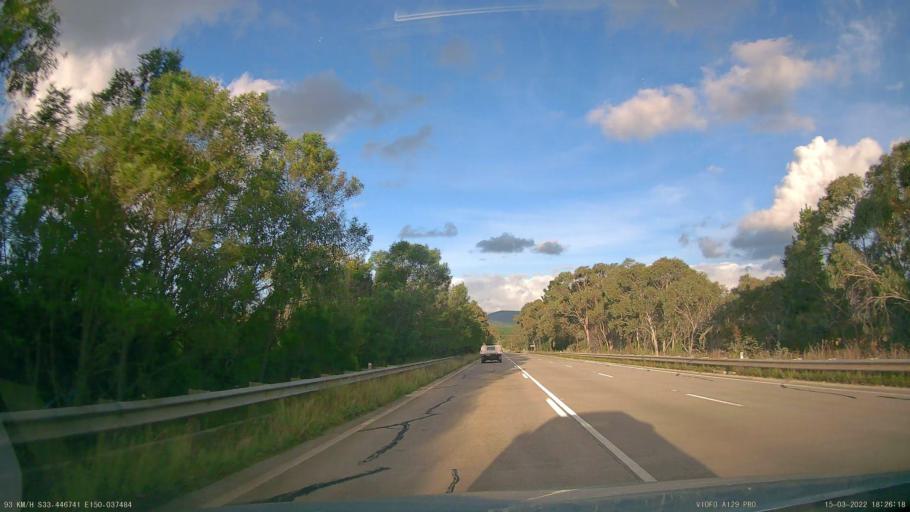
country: AU
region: New South Wales
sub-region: Lithgow
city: Lithgow
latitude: -33.4467
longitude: 150.0380
